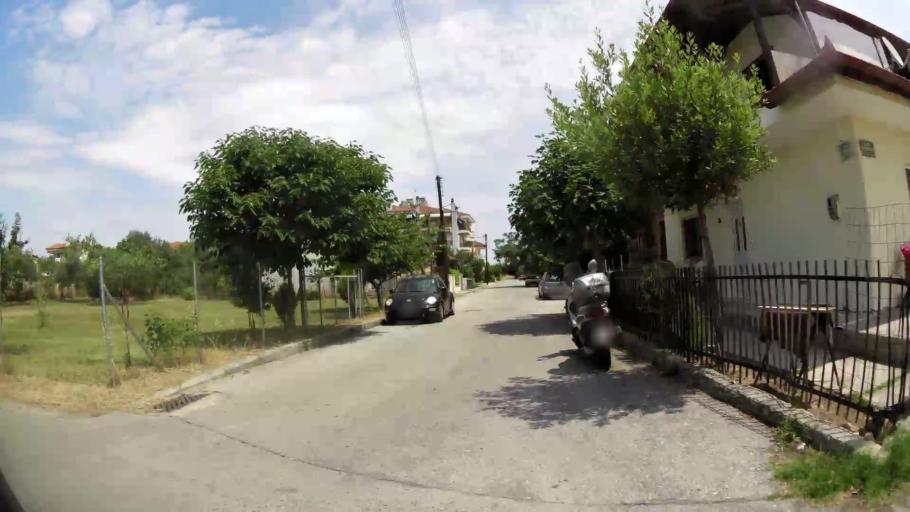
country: GR
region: Central Macedonia
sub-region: Nomos Pierias
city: Katerini
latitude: 40.2625
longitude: 22.5180
